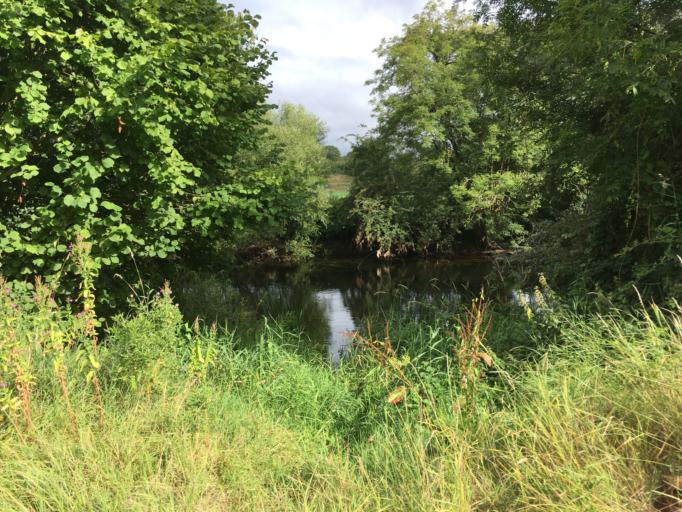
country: IE
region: Munster
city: Cashel
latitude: 52.4732
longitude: -7.9965
